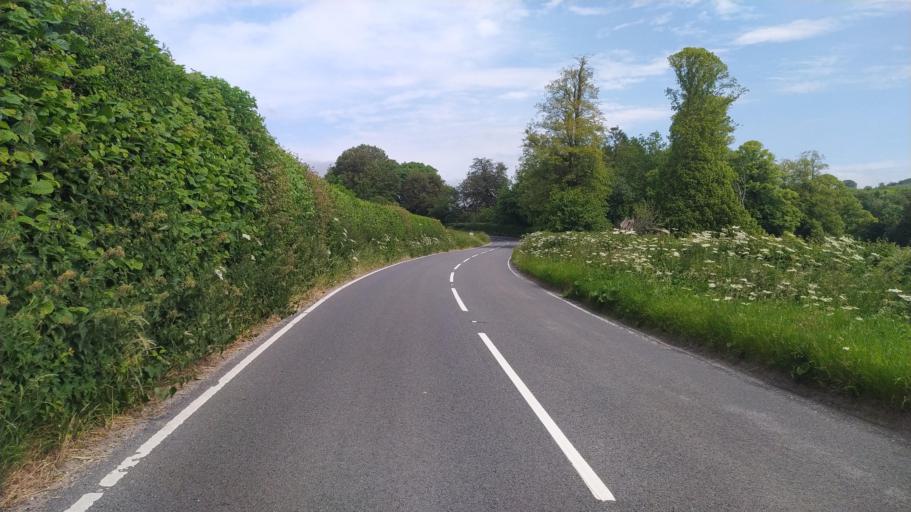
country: GB
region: England
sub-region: Dorset
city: Dorchester
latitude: 50.7816
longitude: -2.4722
